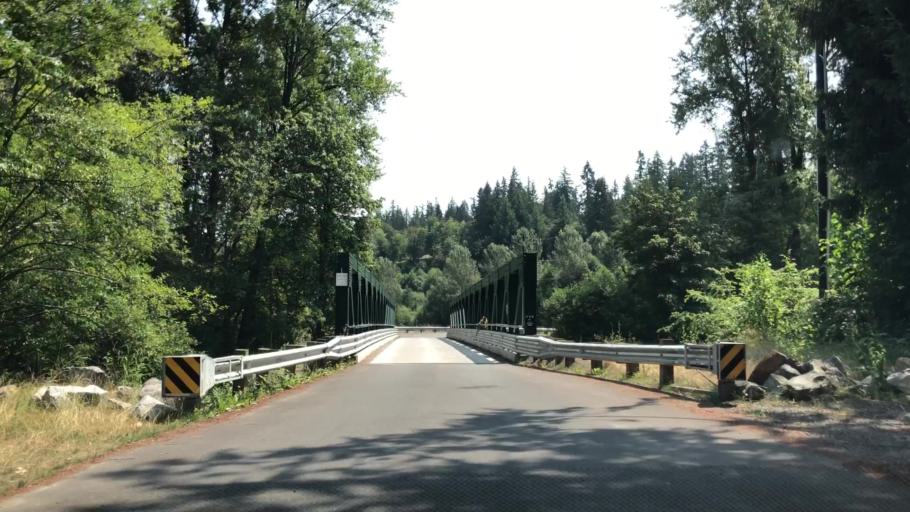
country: US
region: Washington
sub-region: Snohomish County
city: Lochsloy
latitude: 48.0537
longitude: -122.0241
